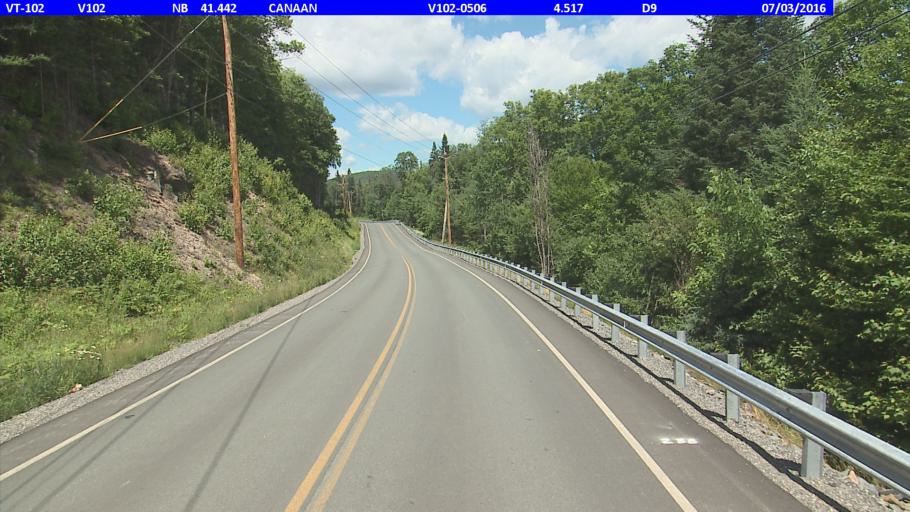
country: US
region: New Hampshire
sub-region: Coos County
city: Colebrook
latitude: 44.9696
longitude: -71.5261
